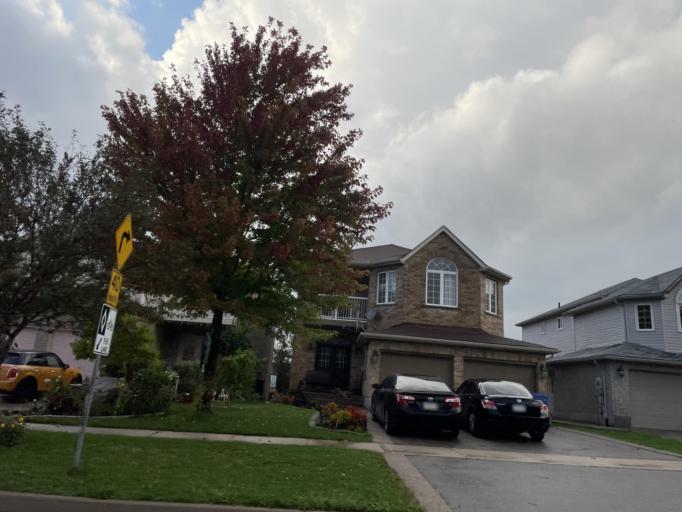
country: CA
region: Ontario
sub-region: Wellington County
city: Guelph
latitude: 43.4941
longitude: -80.1975
